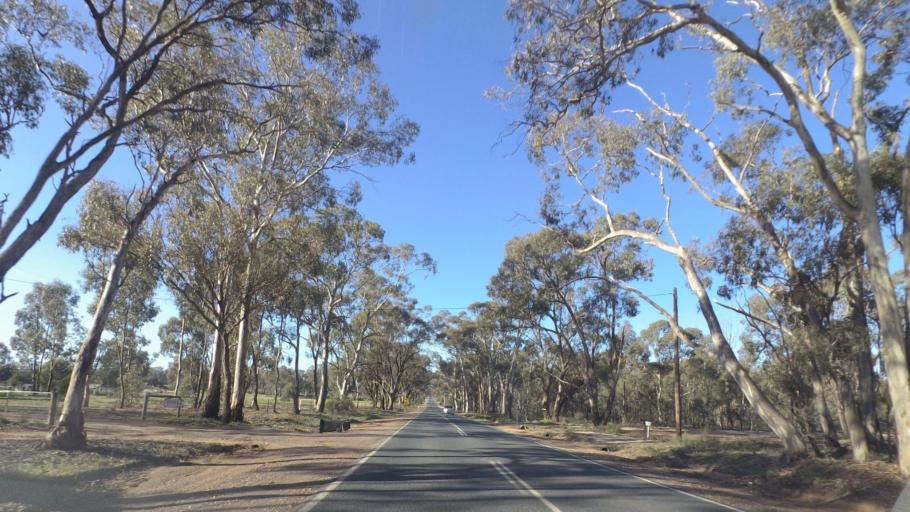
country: AU
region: Victoria
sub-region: Greater Bendigo
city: Epsom
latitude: -36.6761
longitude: 144.3917
